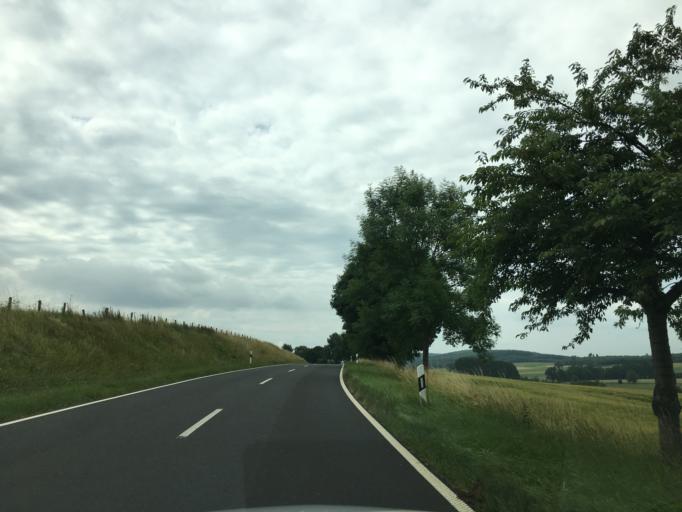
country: DE
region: Hesse
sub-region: Regierungsbezirk Darmstadt
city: Birstein
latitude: 50.3933
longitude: 9.2919
